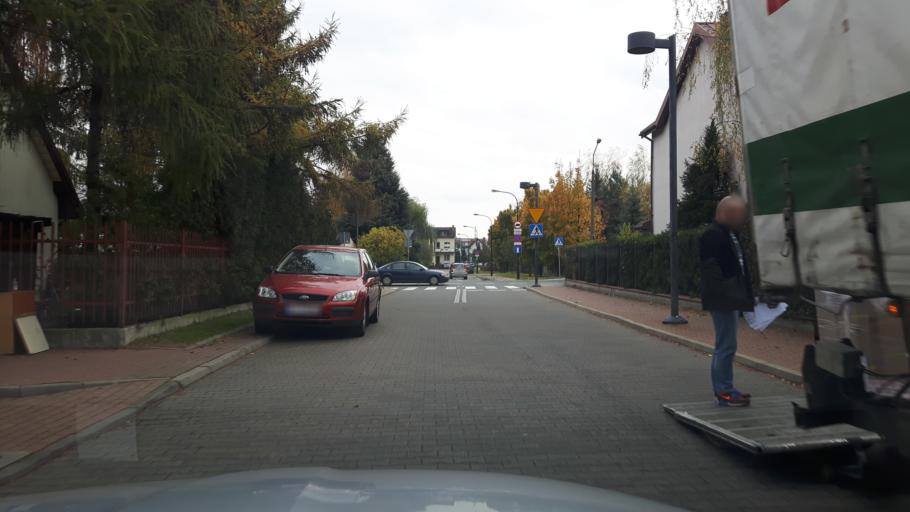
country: PL
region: Masovian Voivodeship
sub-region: Warszawa
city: Targowek
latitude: 52.2848
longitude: 21.0584
